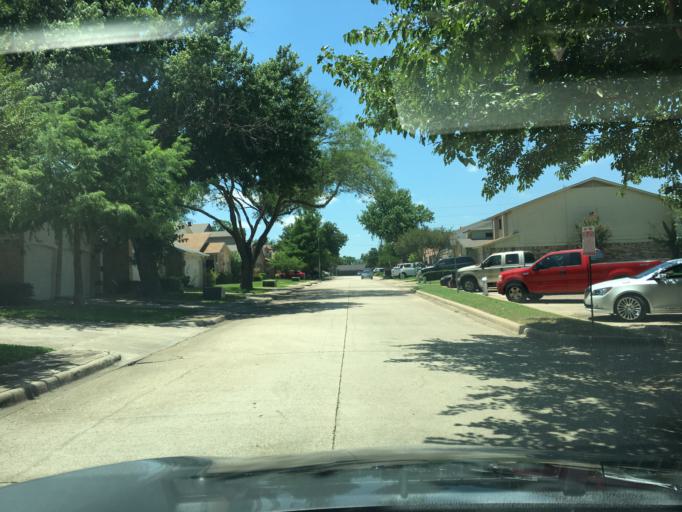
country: US
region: Texas
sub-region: Dallas County
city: Garland
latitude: 32.9486
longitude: -96.6713
